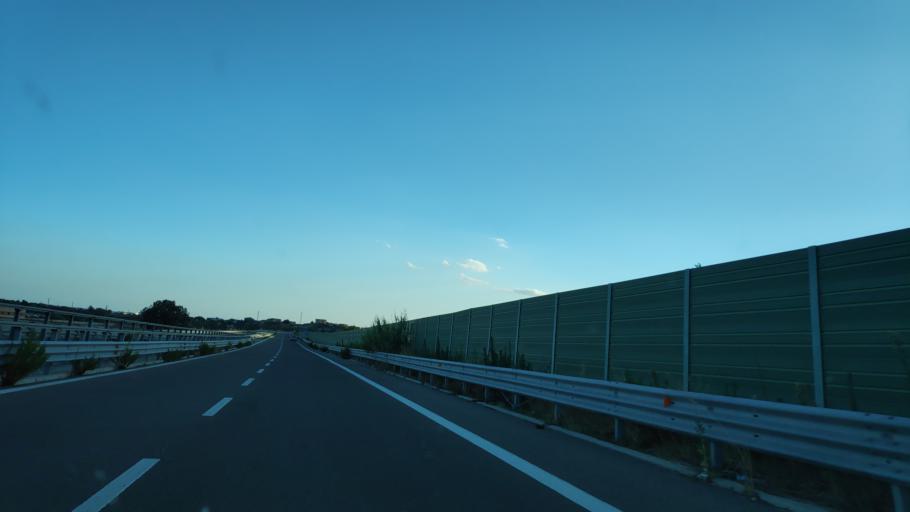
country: IT
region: Calabria
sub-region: Provincia di Reggio Calabria
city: Locri
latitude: 38.2642
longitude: 16.2651
